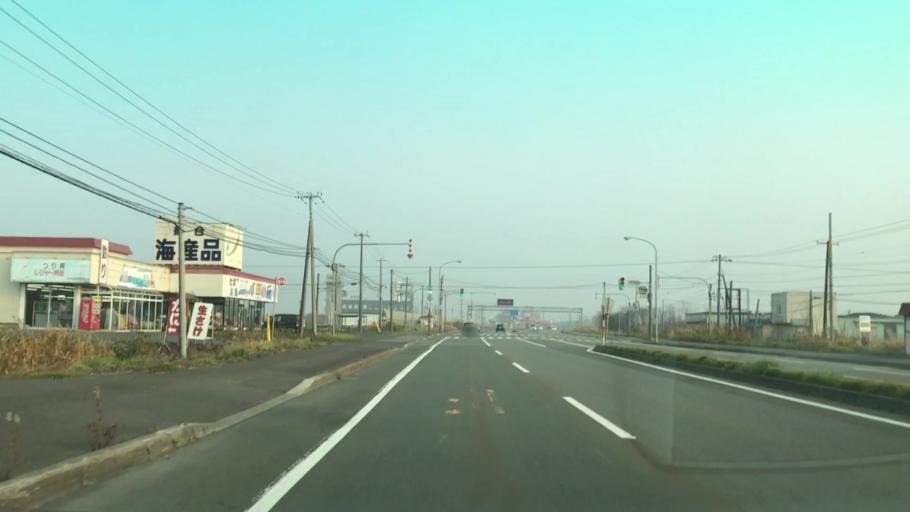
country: JP
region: Hokkaido
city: Ishikari
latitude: 43.2124
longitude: 141.3347
